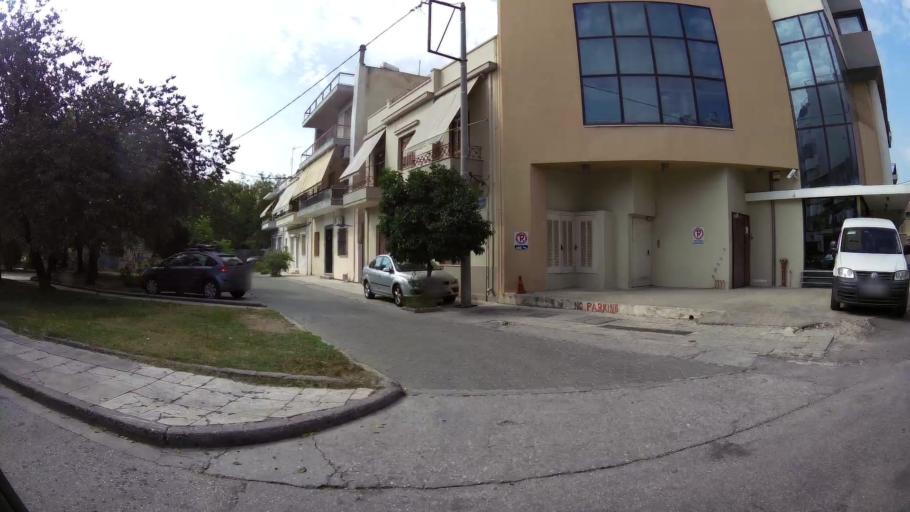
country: GR
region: Attica
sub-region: Nomarchia Athinas
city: Athens
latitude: 37.9951
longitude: 23.7082
